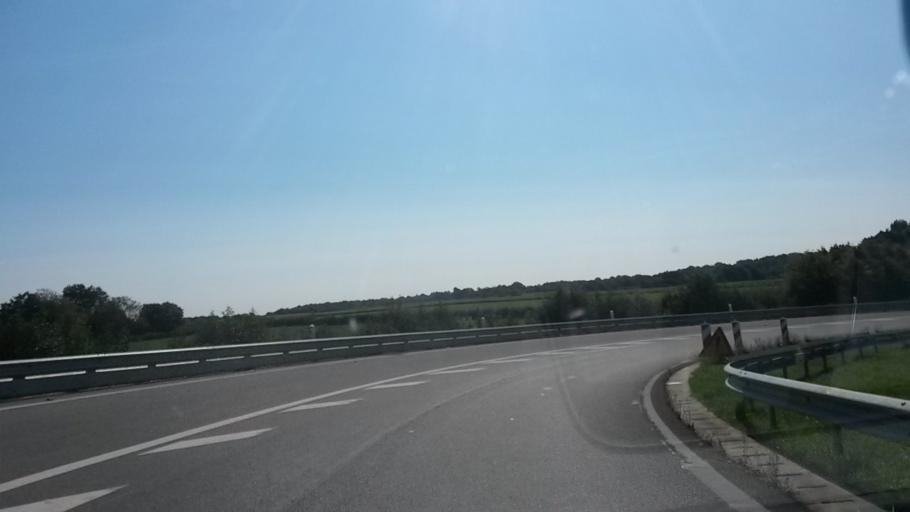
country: FR
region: Nord-Pas-de-Calais
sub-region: Departement du Nord
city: Hautmont
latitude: 50.2073
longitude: 3.9564
